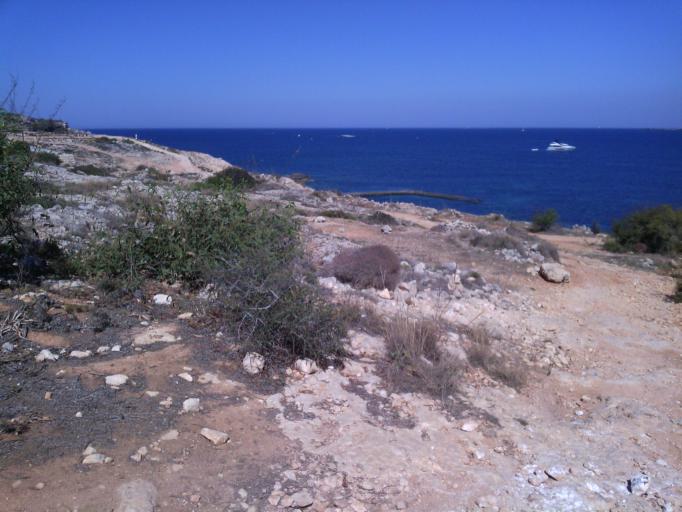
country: MT
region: Il-Mellieha
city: Mellieha
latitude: 35.9798
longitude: 14.3593
